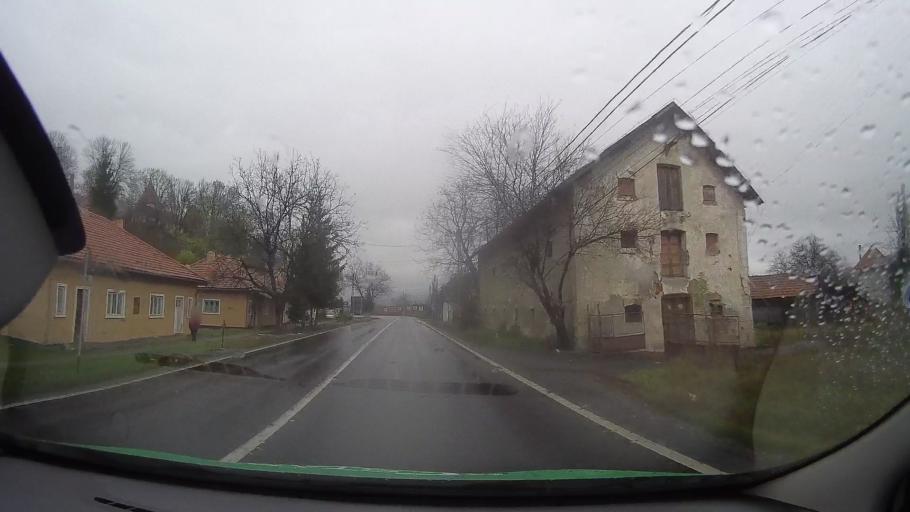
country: RO
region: Mures
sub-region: Comuna Brancovenesti
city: Brancovenesti
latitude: 46.8596
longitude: 24.7665
